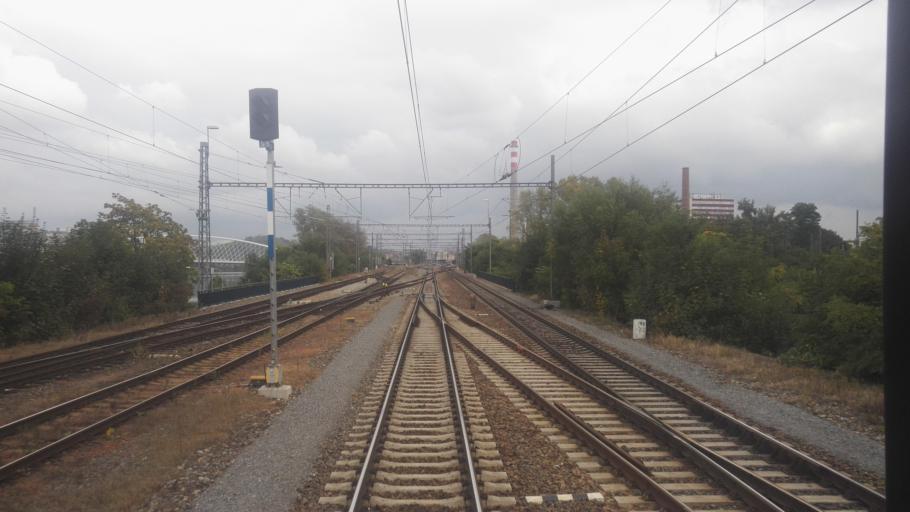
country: CZ
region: Praha
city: Prague
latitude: 50.1100
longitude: 14.4294
